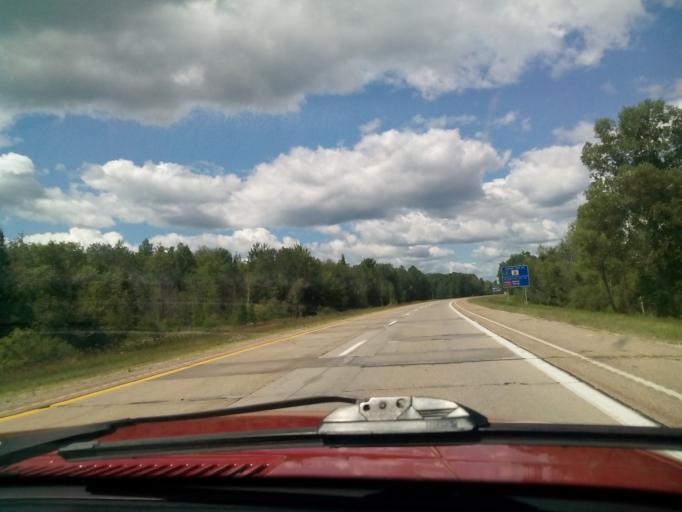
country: US
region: Michigan
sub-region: Ogemaw County
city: West Branch
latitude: 44.2173
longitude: -84.2033
